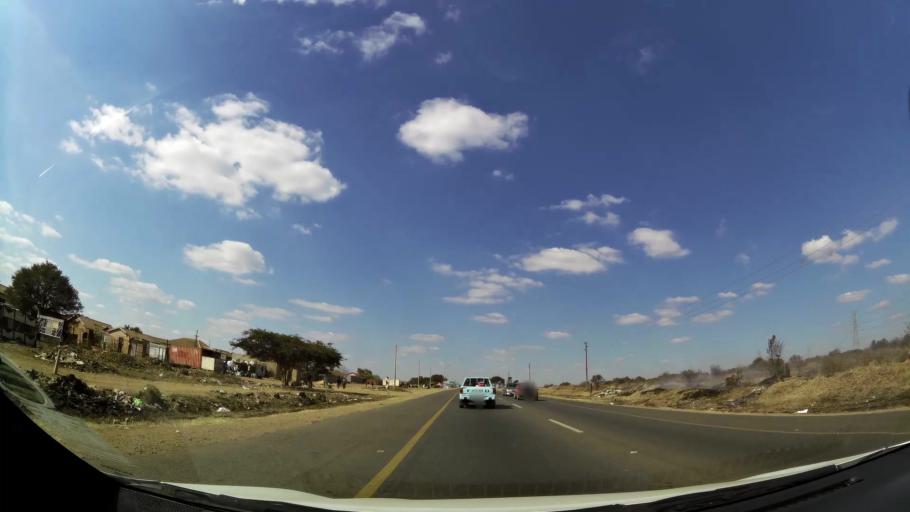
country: ZA
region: Gauteng
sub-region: City of Tshwane Metropolitan Municipality
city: Pretoria
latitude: -25.7437
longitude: 28.3457
